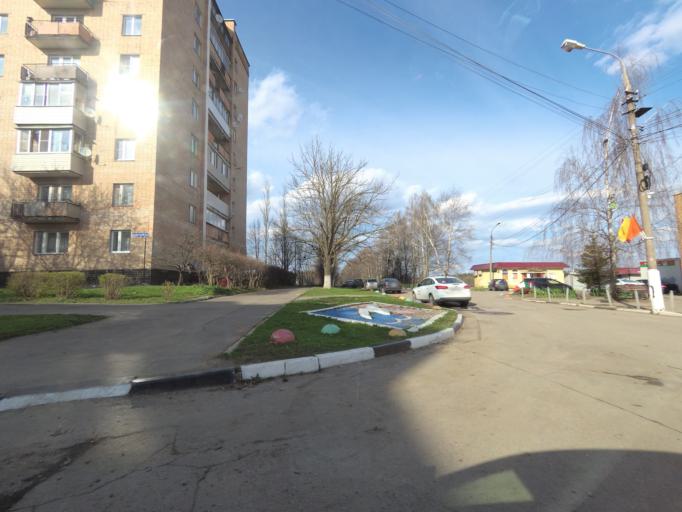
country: RU
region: Moskovskaya
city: Lugovaya
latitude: 56.0455
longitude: 37.4834
